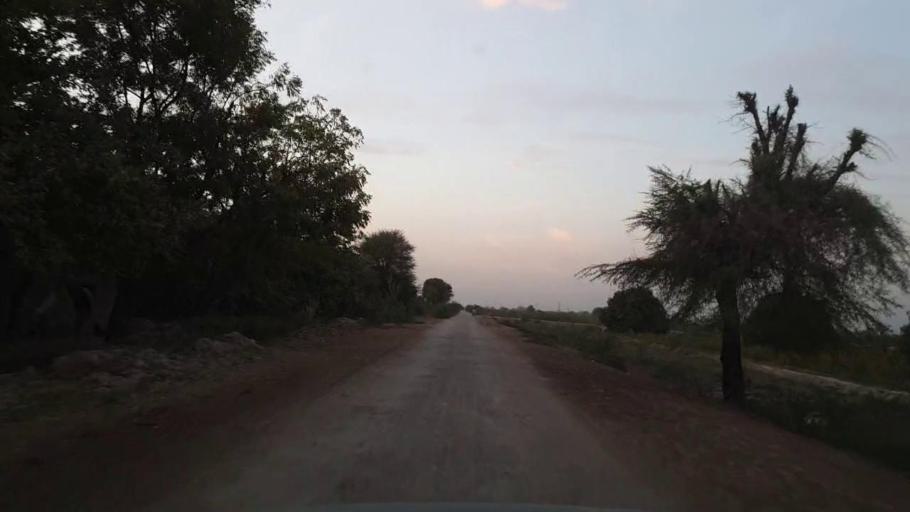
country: PK
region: Sindh
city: Kunri
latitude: 25.1471
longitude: 69.5570
